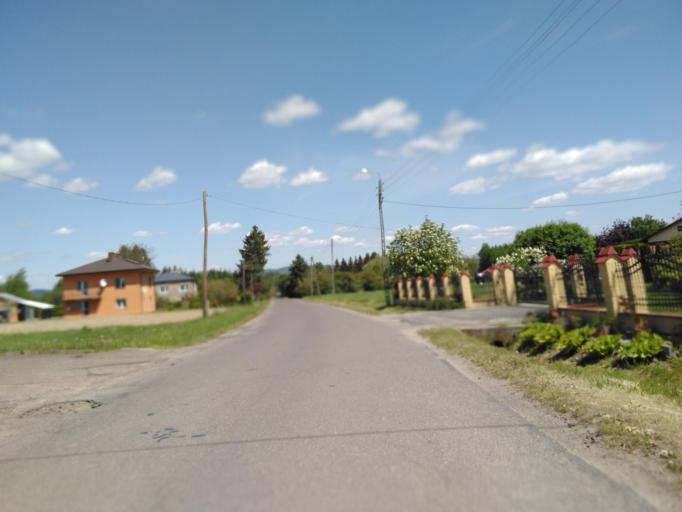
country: PL
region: Subcarpathian Voivodeship
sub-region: Powiat krosnienski
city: Odrzykon
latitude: 49.7111
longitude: 21.7017
